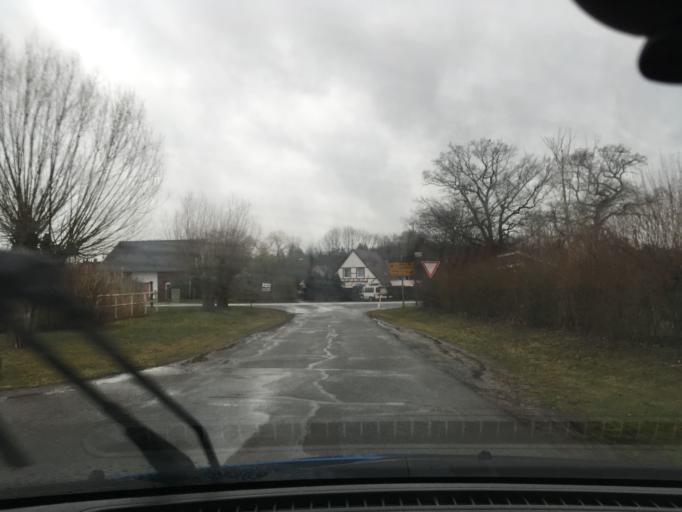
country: DE
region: Schleswig-Holstein
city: Schnakenbek
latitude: 53.3872
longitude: 10.5019
